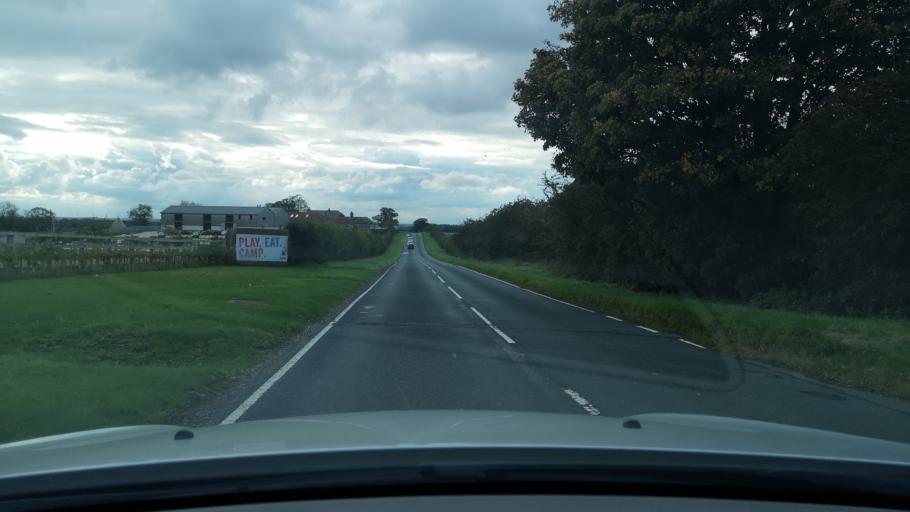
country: GB
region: England
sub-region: East Riding of Yorkshire
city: Hotham
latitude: 53.7897
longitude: -0.6211
